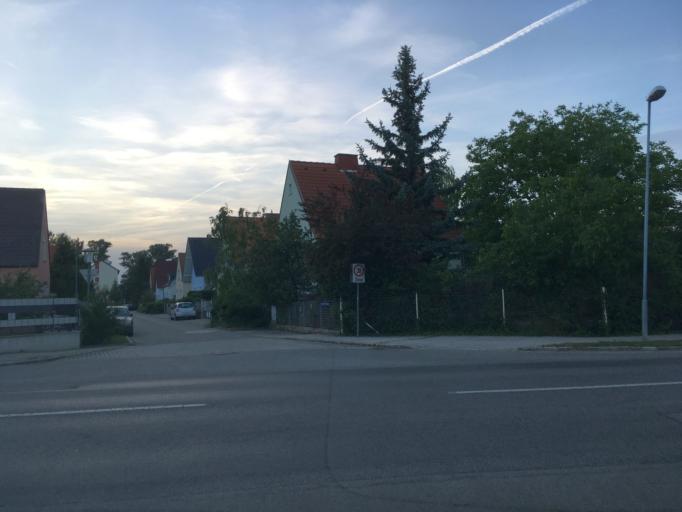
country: AT
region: Lower Austria
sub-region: Politischer Bezirk Baden
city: Teesdorf
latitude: 47.9479
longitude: 16.2811
